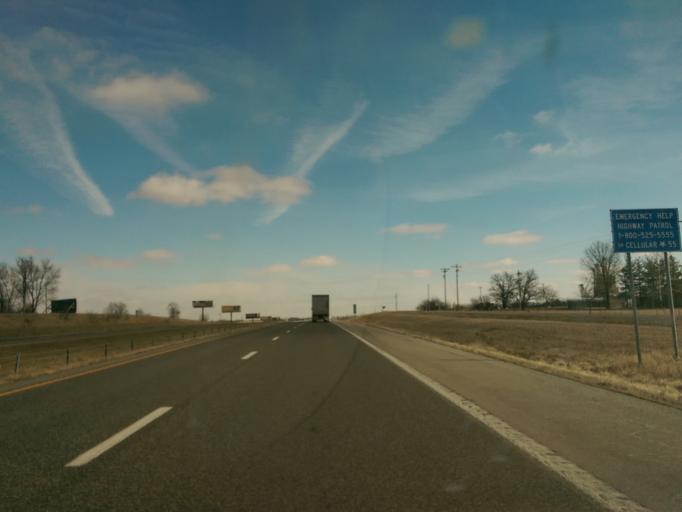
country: US
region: Missouri
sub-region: Callaway County
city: Fulton
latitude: 38.9438
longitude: -91.9026
